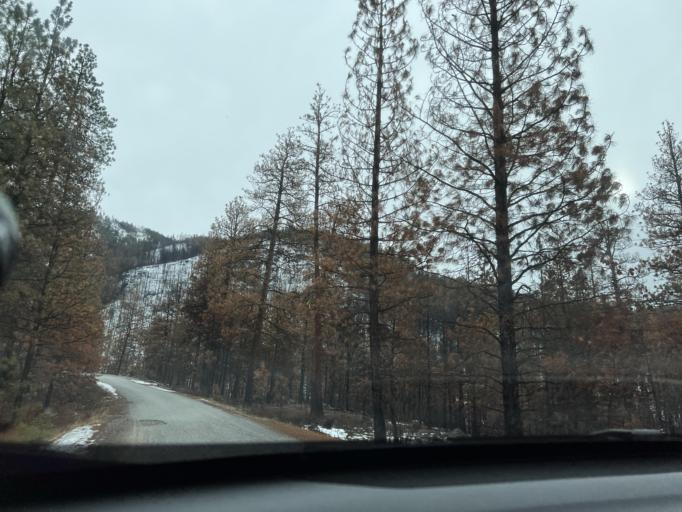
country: US
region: Washington
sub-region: Okanogan County
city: Brewster
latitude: 48.5791
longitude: -120.1610
